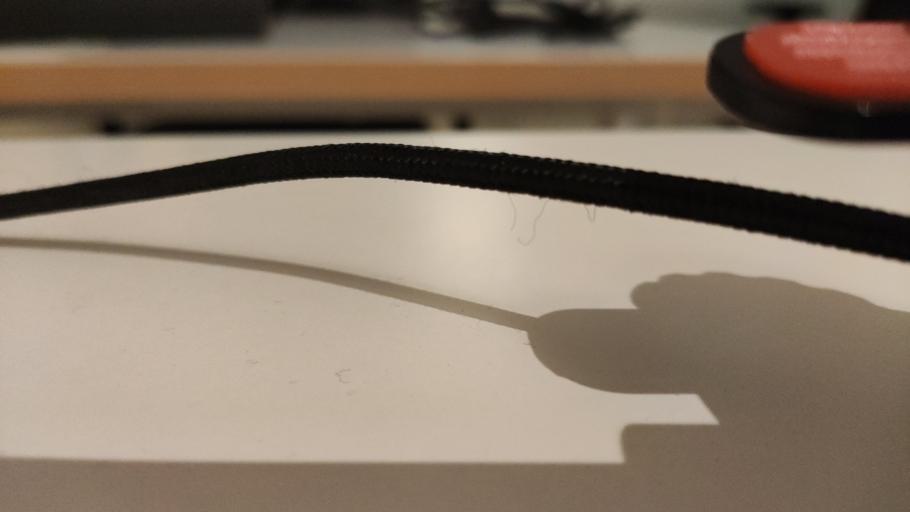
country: RU
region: Moskovskaya
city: Bogorodskoye
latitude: 56.4356
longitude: 37.8662
